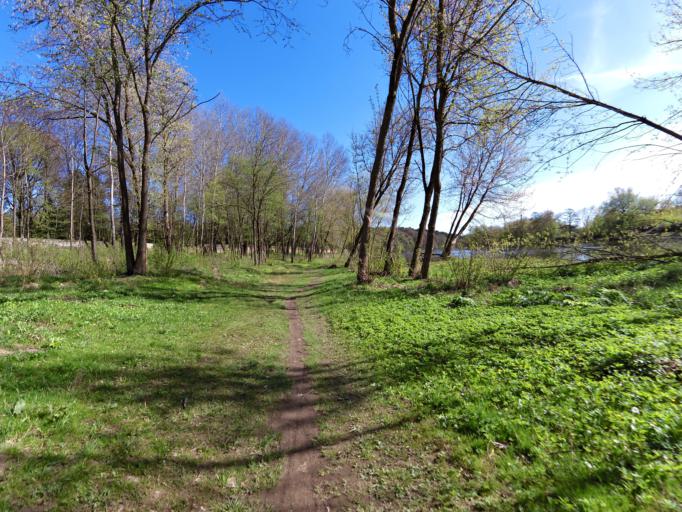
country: LT
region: Vilnius County
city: Vilkpede
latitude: 54.6837
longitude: 25.2290
